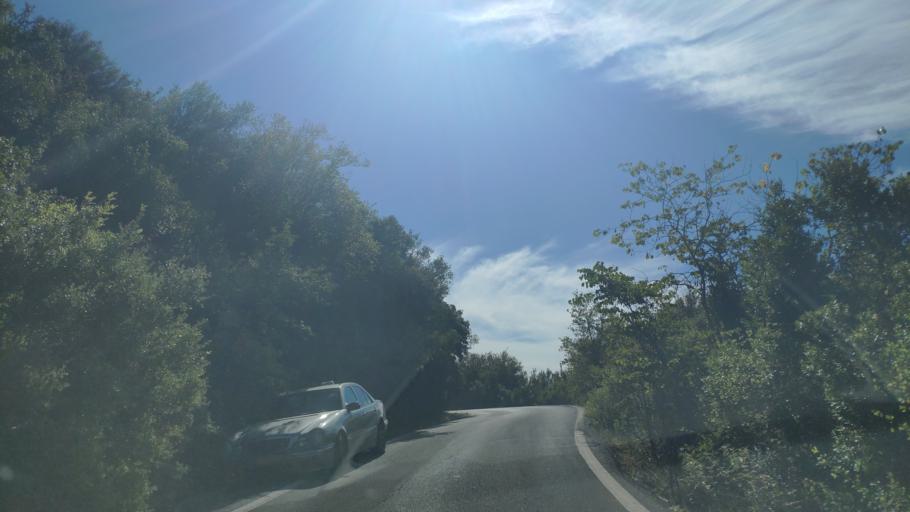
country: GR
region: Peloponnese
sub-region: Nomos Arkadias
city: Dimitsana
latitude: 37.5359
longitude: 22.0489
